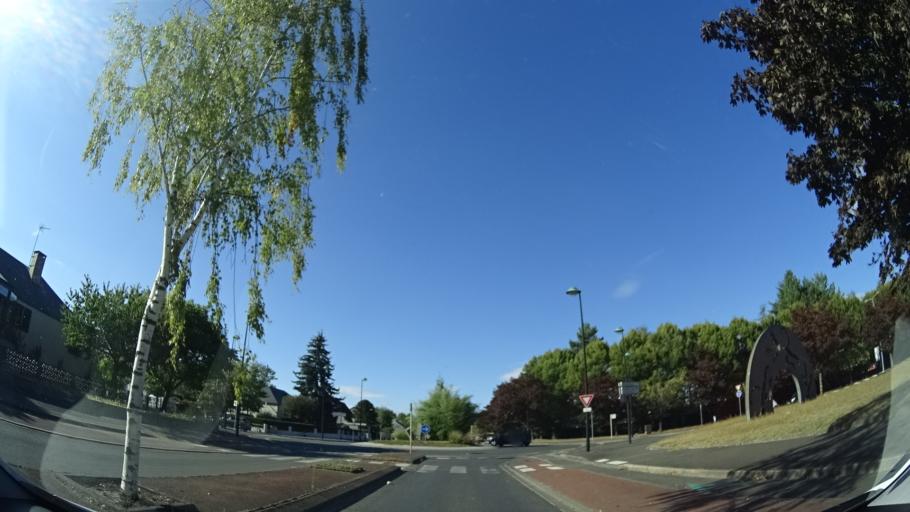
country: FR
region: Centre
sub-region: Departement du Loiret
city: Saint-Jean-de-Braye
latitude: 47.9141
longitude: 1.9781
